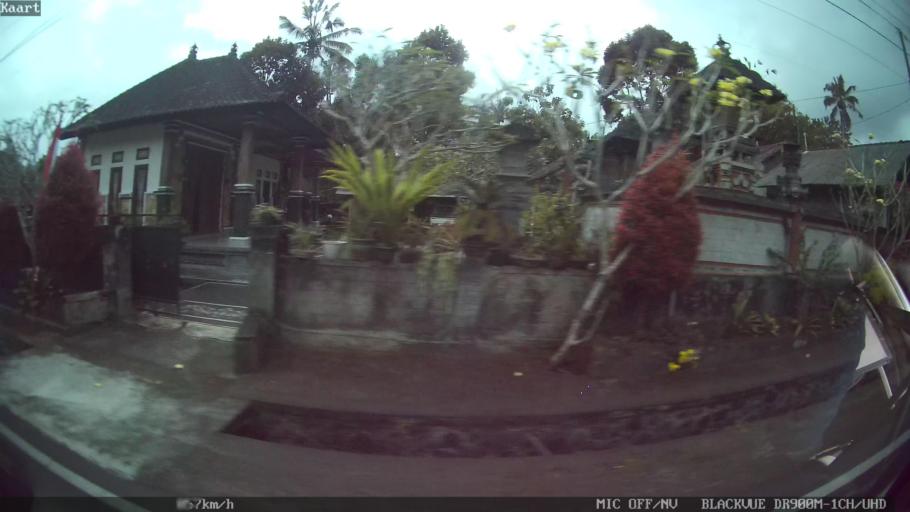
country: ID
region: Bali
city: Banjar Tiga
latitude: -8.3795
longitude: 115.4178
